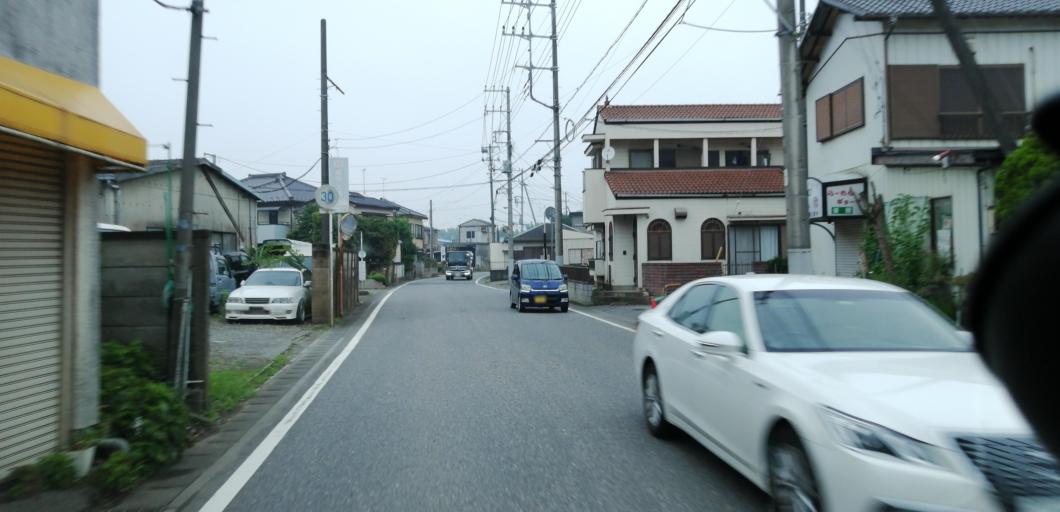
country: JP
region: Ibaraki
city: Iwai
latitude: 36.0130
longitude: 139.8476
